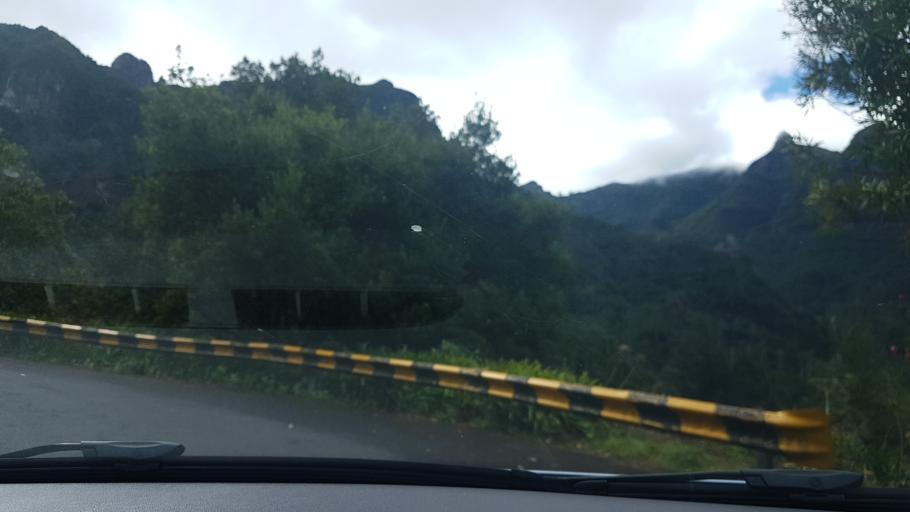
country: PT
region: Madeira
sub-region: Sao Vicente
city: Sao Vicente
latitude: 32.7695
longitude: -17.0276
